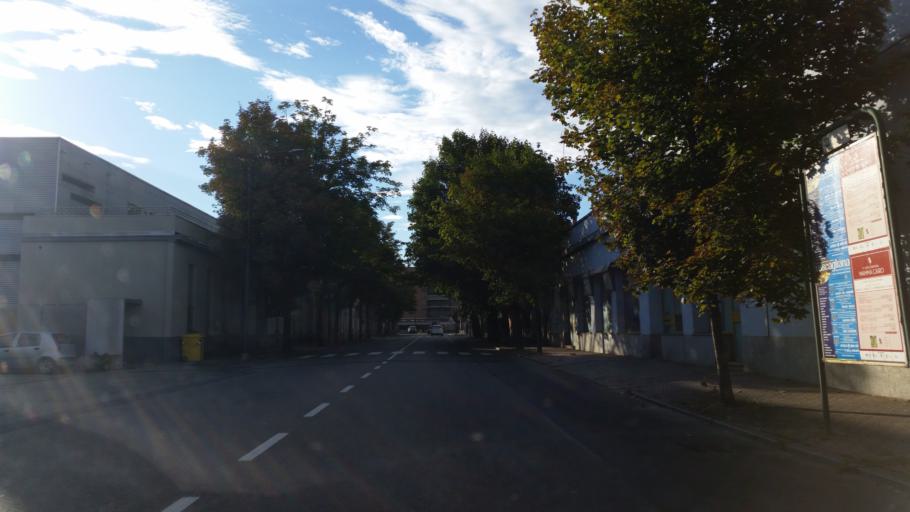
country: IT
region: Piedmont
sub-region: Provincia di Asti
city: Asti
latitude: 44.8956
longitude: 8.1952
